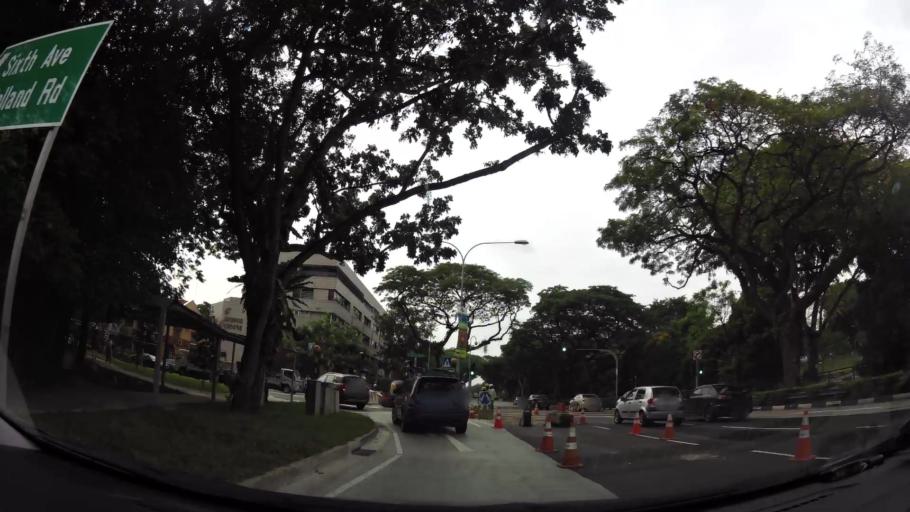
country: SG
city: Singapore
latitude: 1.3314
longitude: 103.7958
